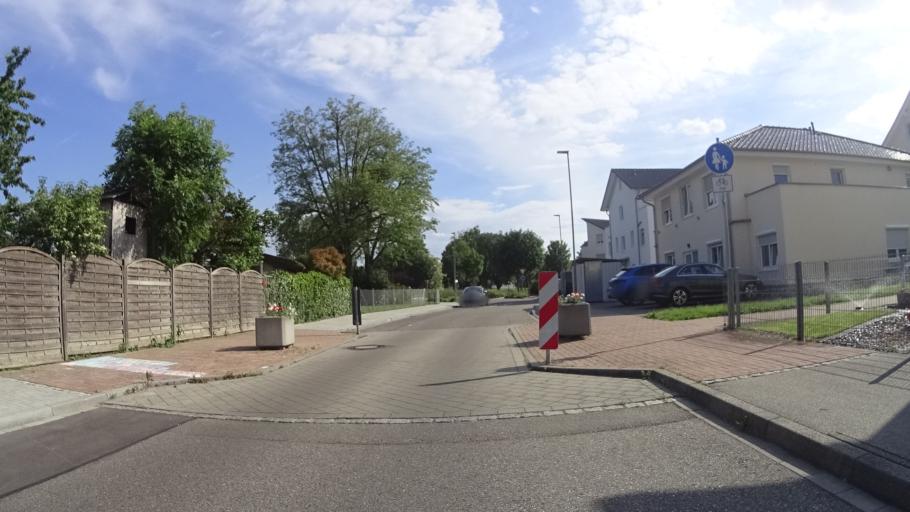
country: DE
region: Baden-Wuerttemberg
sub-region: Freiburg Region
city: Breisach am Rhein
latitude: 48.0393
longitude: 7.5840
